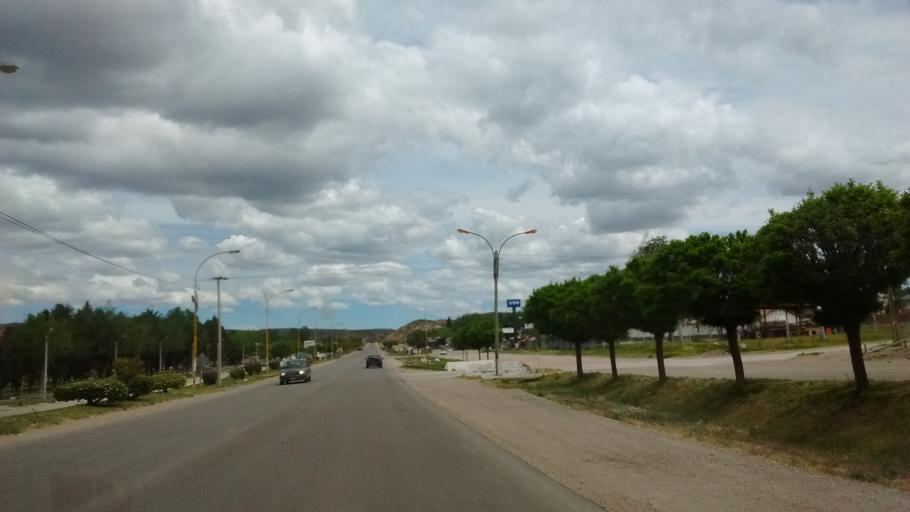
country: AR
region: Neuquen
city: Piedra del Aguila
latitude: -40.0471
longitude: -70.0748
